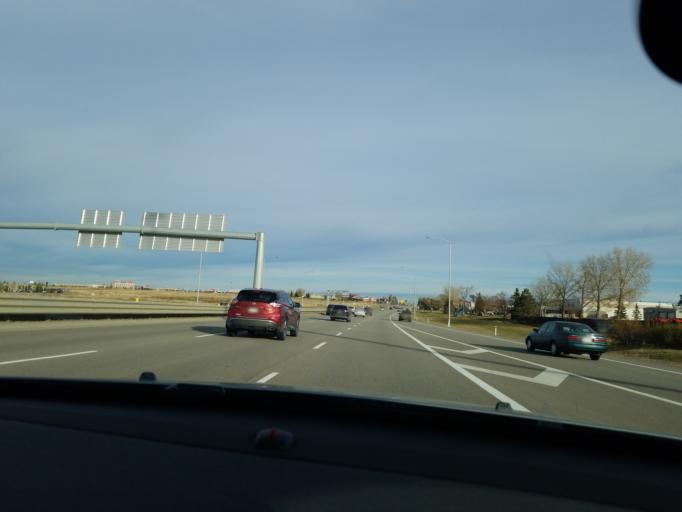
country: CA
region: Alberta
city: Sherwood Park
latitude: 53.5410
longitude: -113.3322
